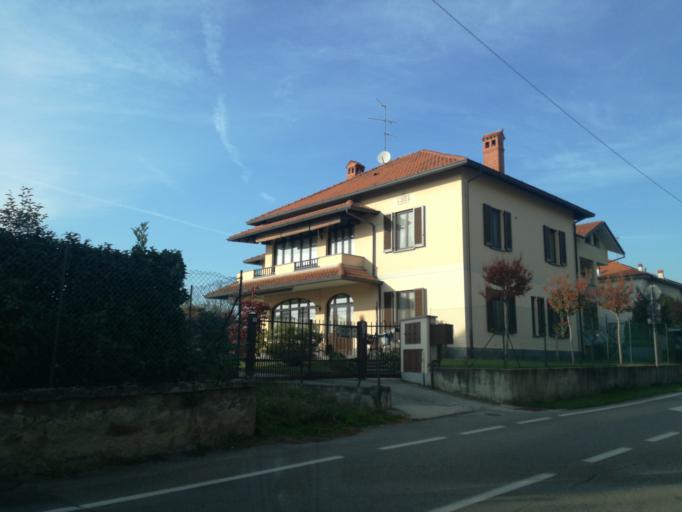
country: IT
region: Lombardy
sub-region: Provincia di Monza e Brianza
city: Aicurzio
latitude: 45.6413
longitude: 9.4163
